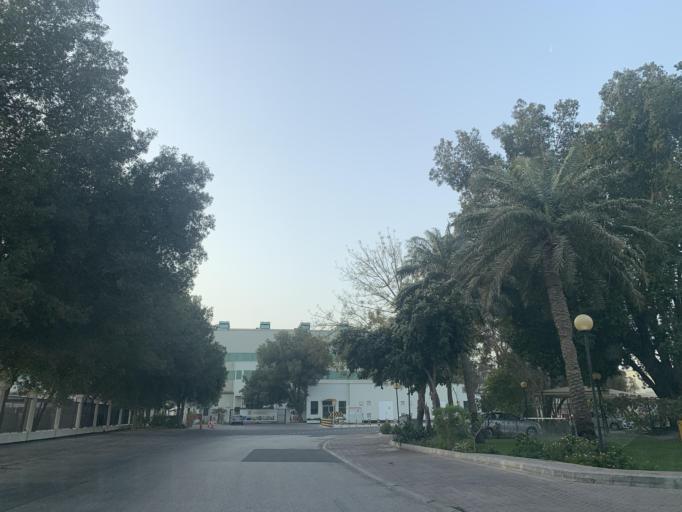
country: BH
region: Manama
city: Manama
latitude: 26.1981
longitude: 50.5983
